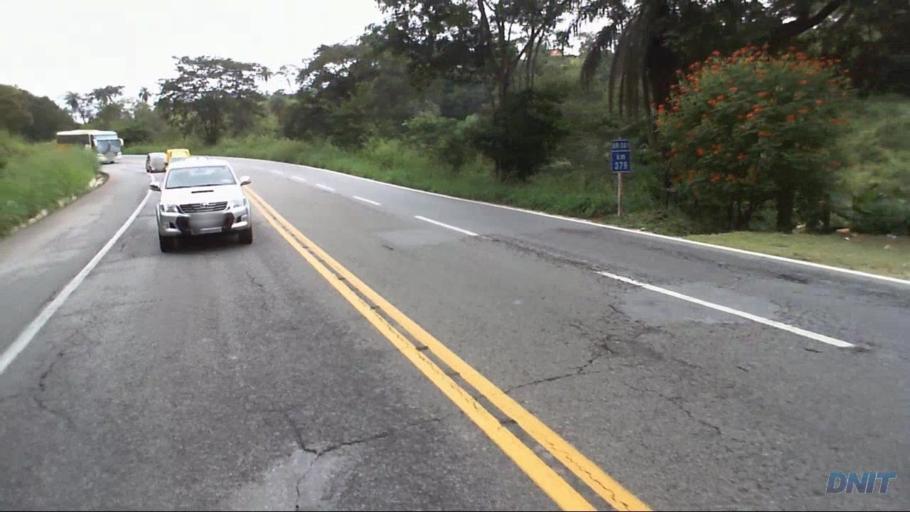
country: BR
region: Minas Gerais
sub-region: Joao Monlevade
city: Joao Monlevade
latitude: -19.8382
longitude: -43.3389
